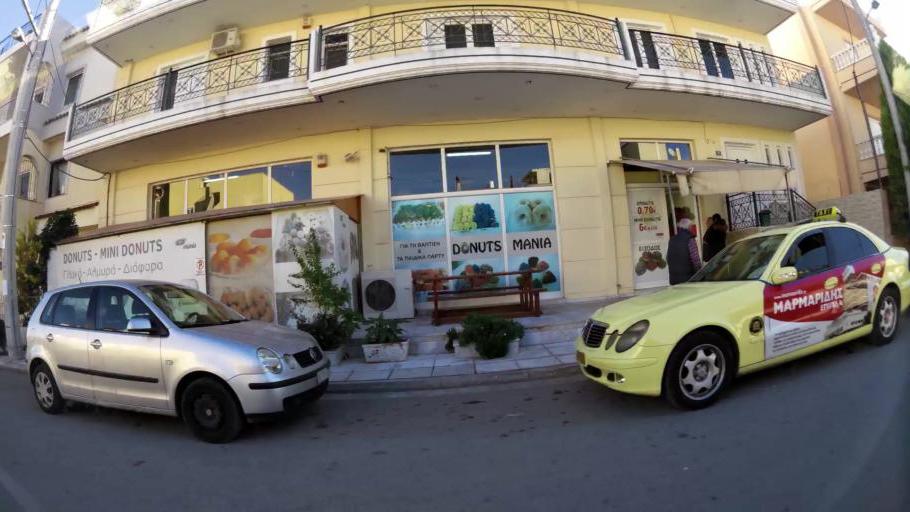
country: GR
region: Attica
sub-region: Nomarchia Anatolikis Attikis
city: Acharnes
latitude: 38.0875
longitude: 23.7288
